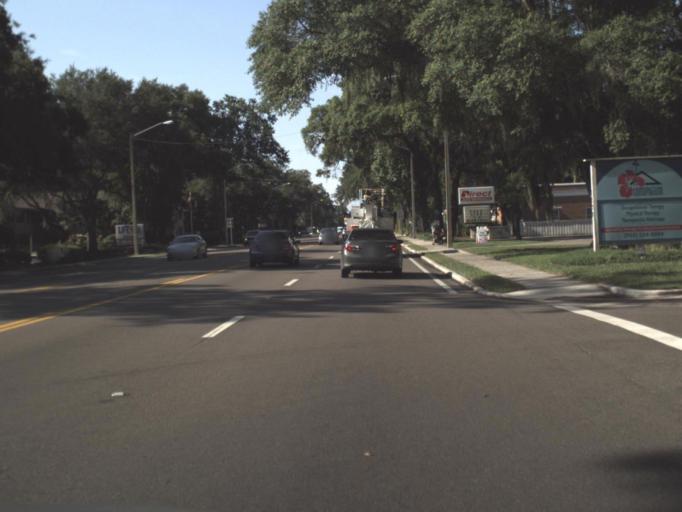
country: US
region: Florida
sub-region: Alachua County
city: Gainesville
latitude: 29.6652
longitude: -82.3392
